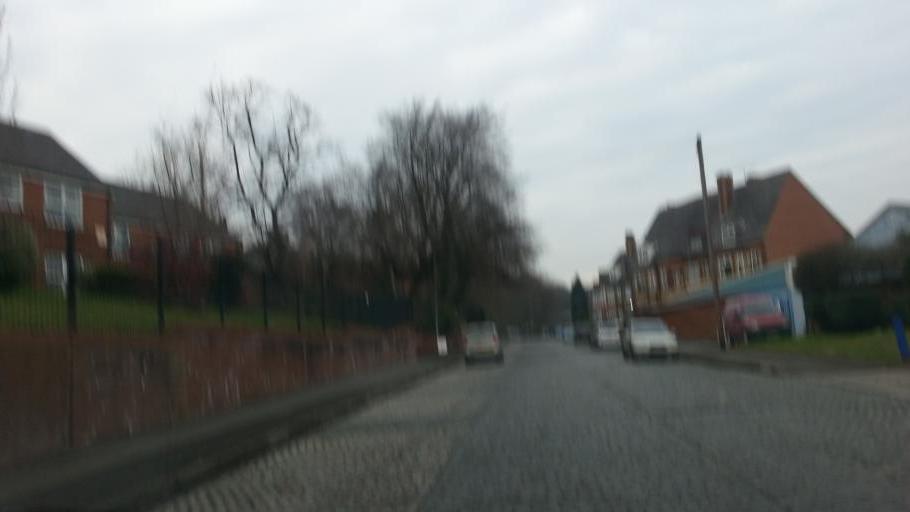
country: GB
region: England
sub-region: Manchester
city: Crumpsall
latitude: 53.5064
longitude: -2.2635
